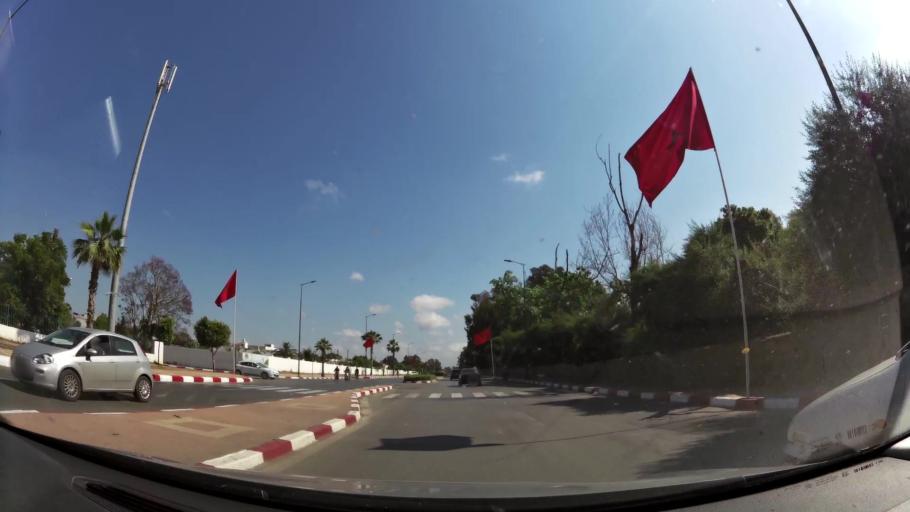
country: MA
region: Rabat-Sale-Zemmour-Zaer
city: Sale
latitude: 34.0400
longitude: -6.7751
